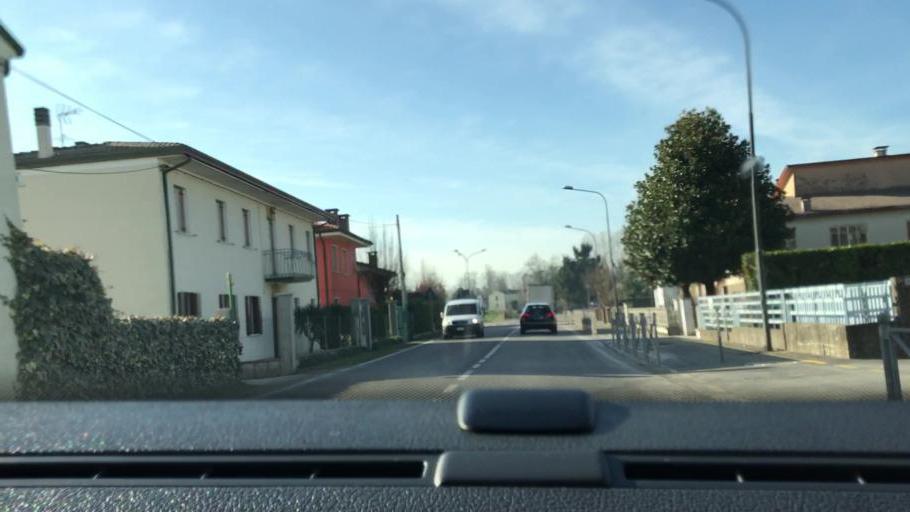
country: IT
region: Veneto
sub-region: Provincia di Rovigo
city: Baruchella
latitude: 45.0676
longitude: 11.4558
